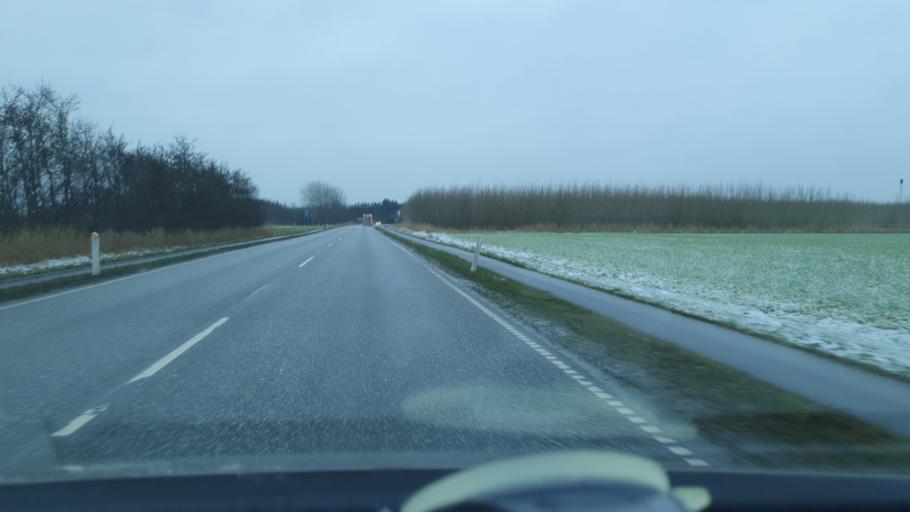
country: DK
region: North Denmark
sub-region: Jammerbugt Kommune
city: Brovst
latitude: 57.1144
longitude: 9.6017
